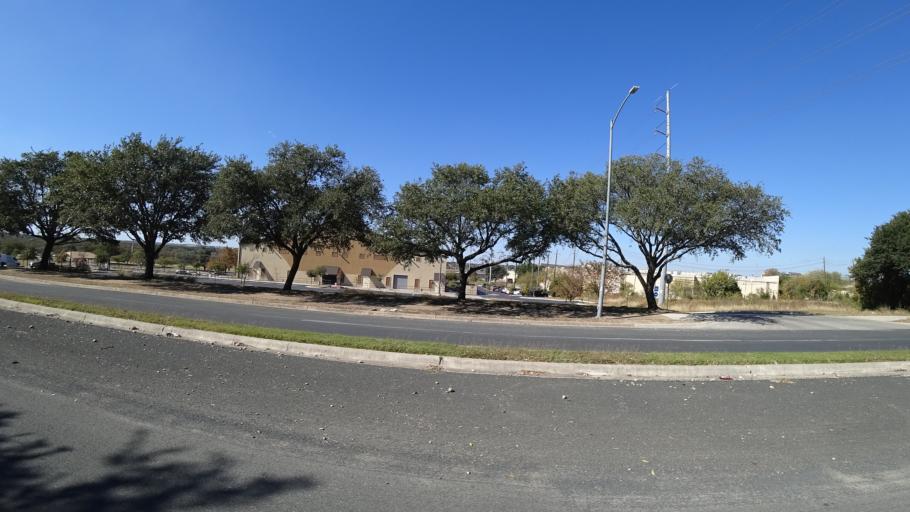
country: US
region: Texas
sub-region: Travis County
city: Wells Branch
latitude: 30.4362
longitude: -97.6963
